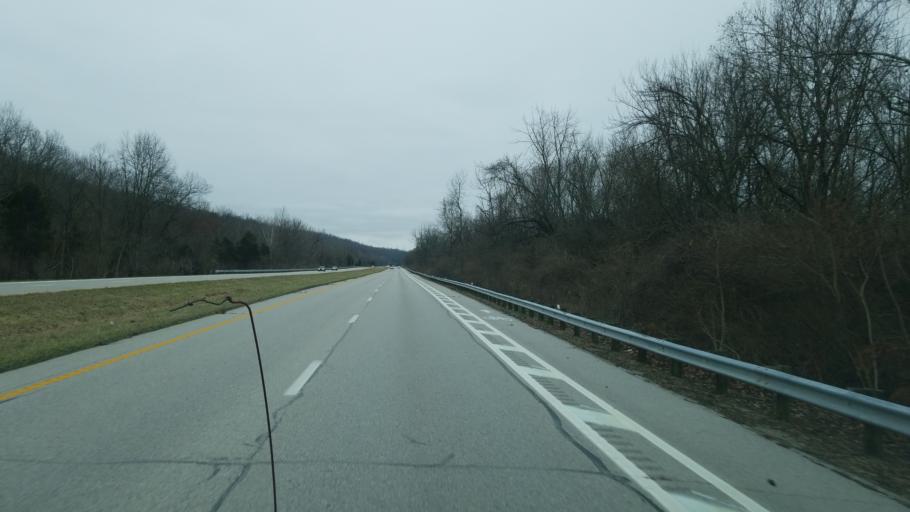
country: US
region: Ohio
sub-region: Clermont County
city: Withamsville
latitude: 39.0210
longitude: -84.3145
